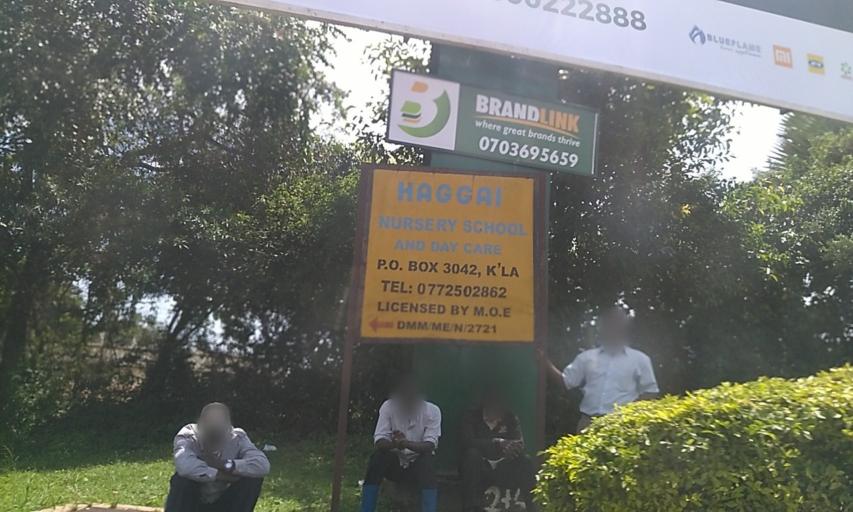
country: UG
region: Central Region
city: Kampala Central Division
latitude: 0.3396
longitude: 32.5903
